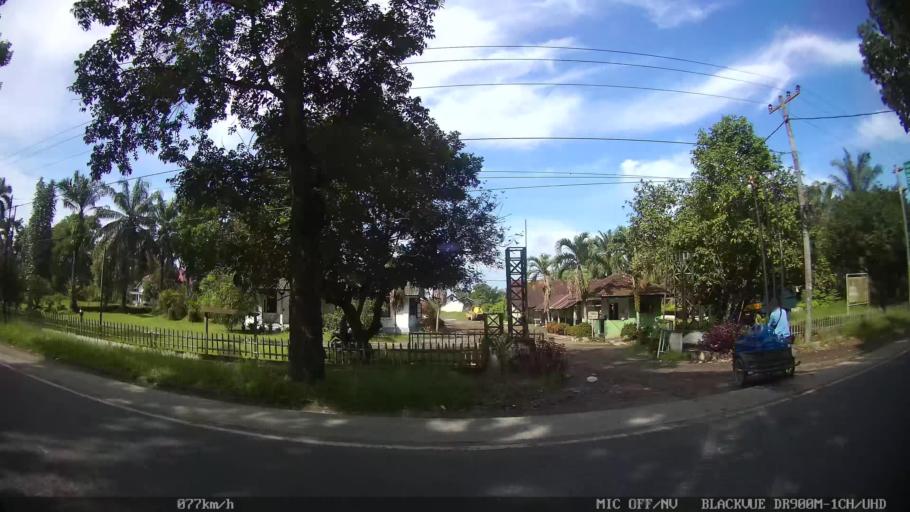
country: ID
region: North Sumatra
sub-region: Kabupaten Langkat
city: Stabat
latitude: 3.7317
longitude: 98.4928
